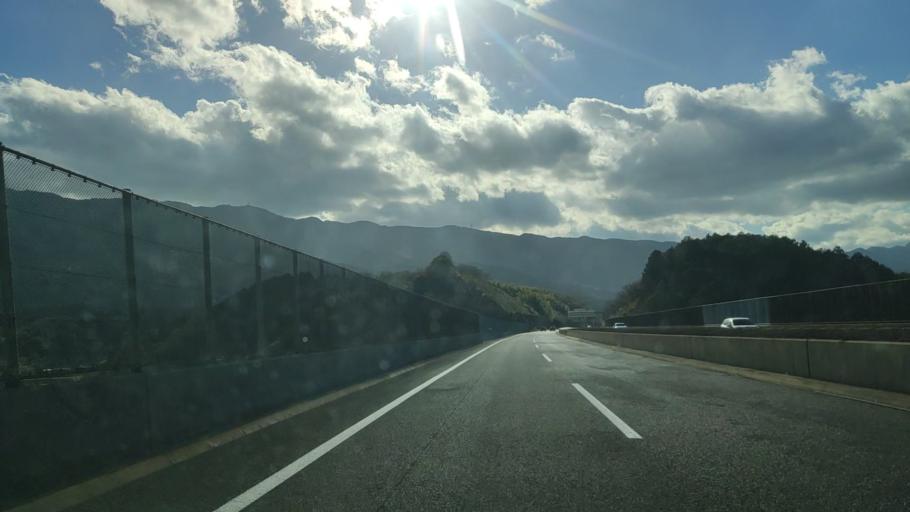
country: JP
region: Ehime
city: Kawanoecho
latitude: 33.9912
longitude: 133.5939
